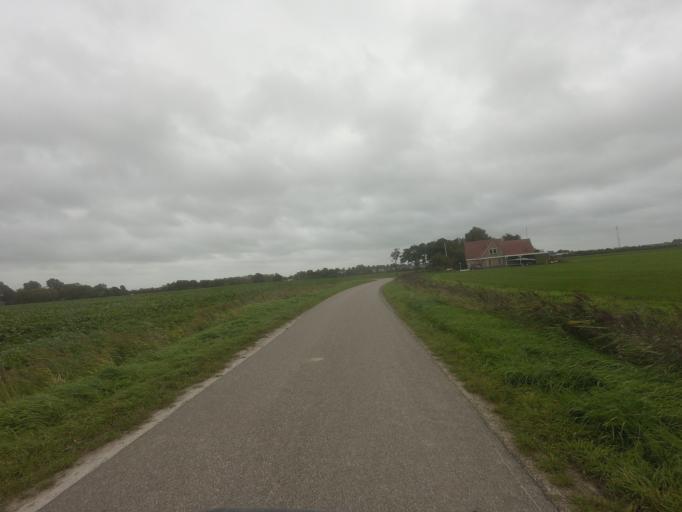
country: NL
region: Friesland
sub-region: Gemeente Leeuwarderadeel
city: Stiens
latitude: 53.2720
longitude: 5.7520
